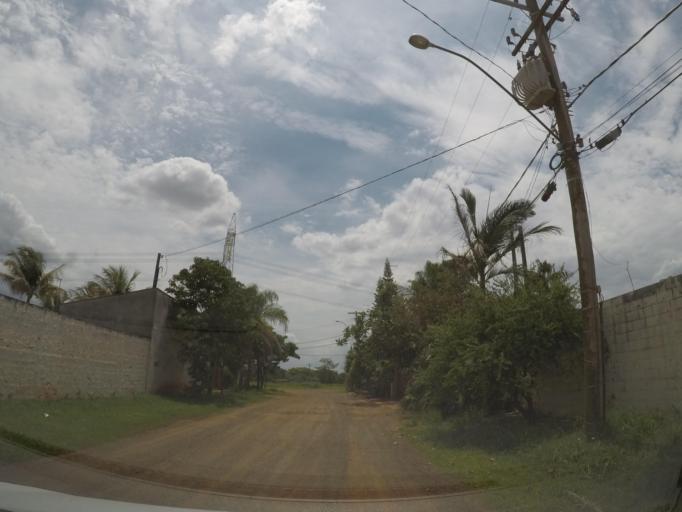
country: BR
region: Sao Paulo
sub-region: Sumare
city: Sumare
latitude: -22.8479
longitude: -47.2956
